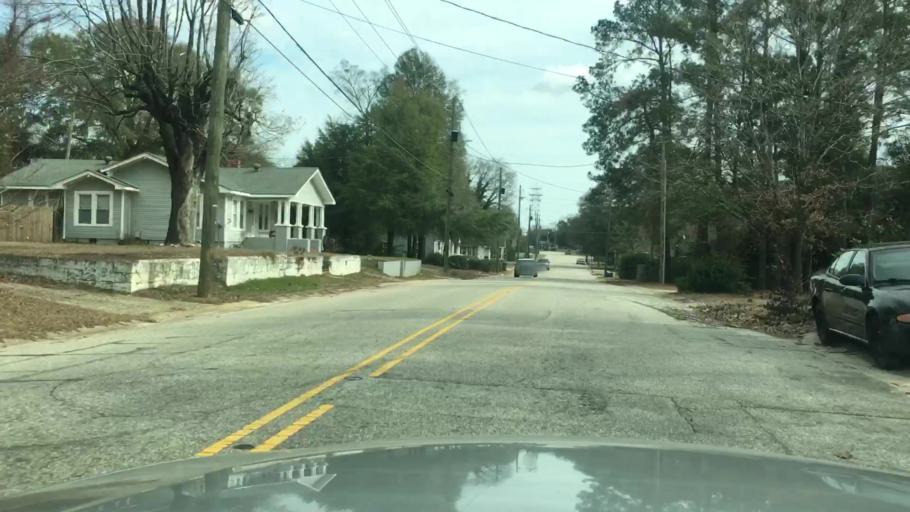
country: US
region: North Carolina
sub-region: Cumberland County
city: Fayetteville
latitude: 35.0526
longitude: -78.8979
